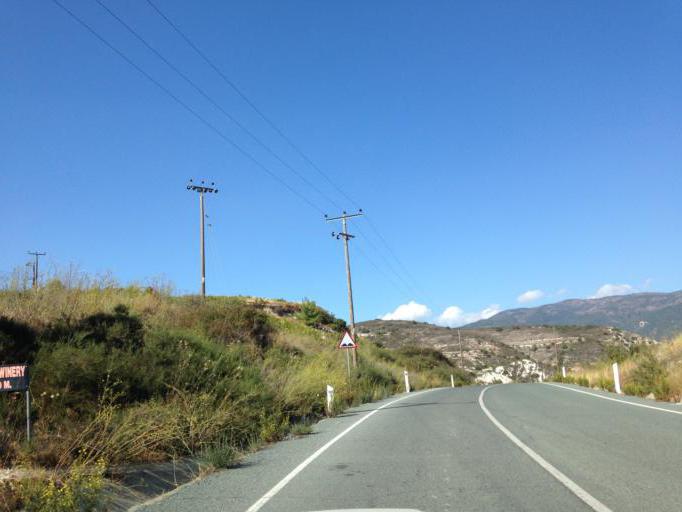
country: CY
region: Limassol
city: Pachna
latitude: 34.8556
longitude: 32.8064
